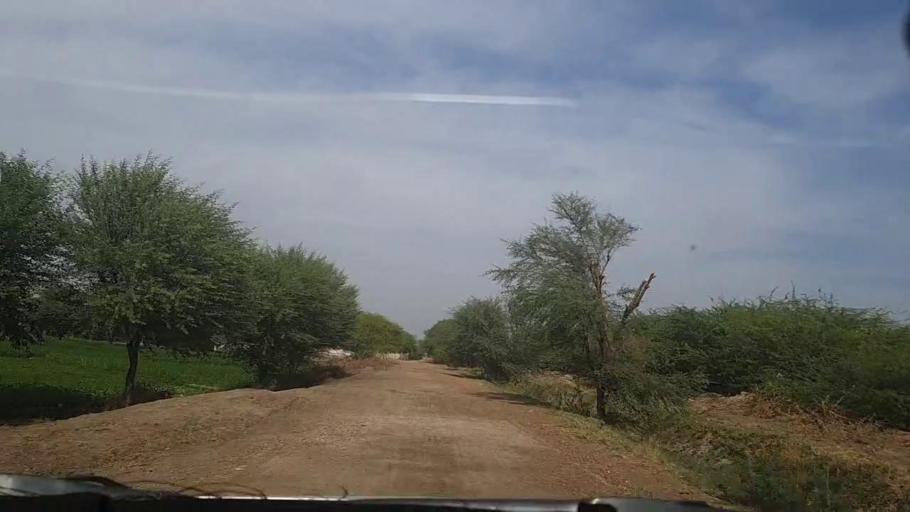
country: PK
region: Sindh
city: Pithoro
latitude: 25.5484
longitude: 69.3647
